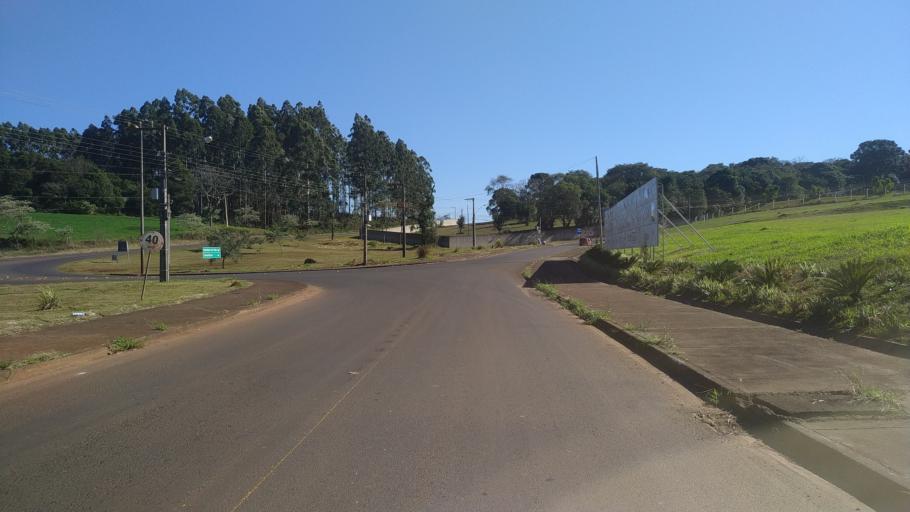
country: BR
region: Santa Catarina
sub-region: Chapeco
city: Chapeco
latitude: -27.1603
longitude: -52.6052
